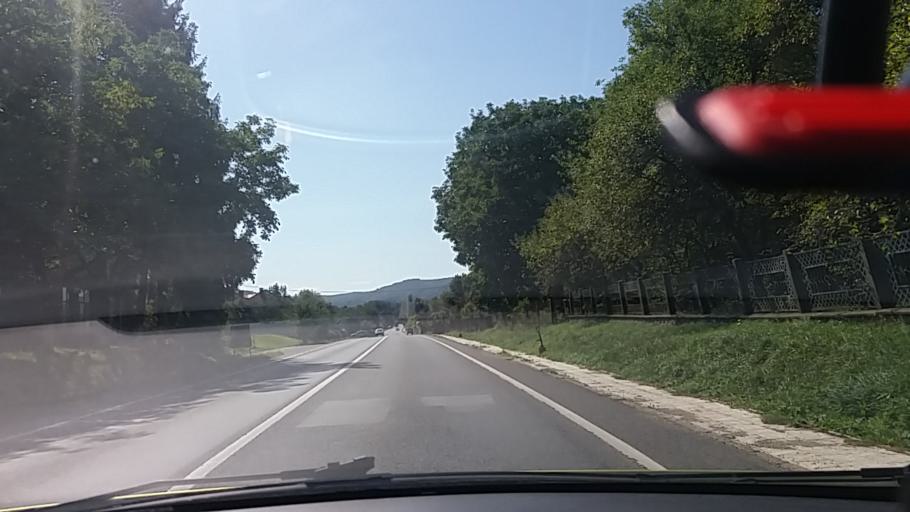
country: RO
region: Hunedoara
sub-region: Comuna Zam
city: Zam
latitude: 46.0050
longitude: 22.4427
